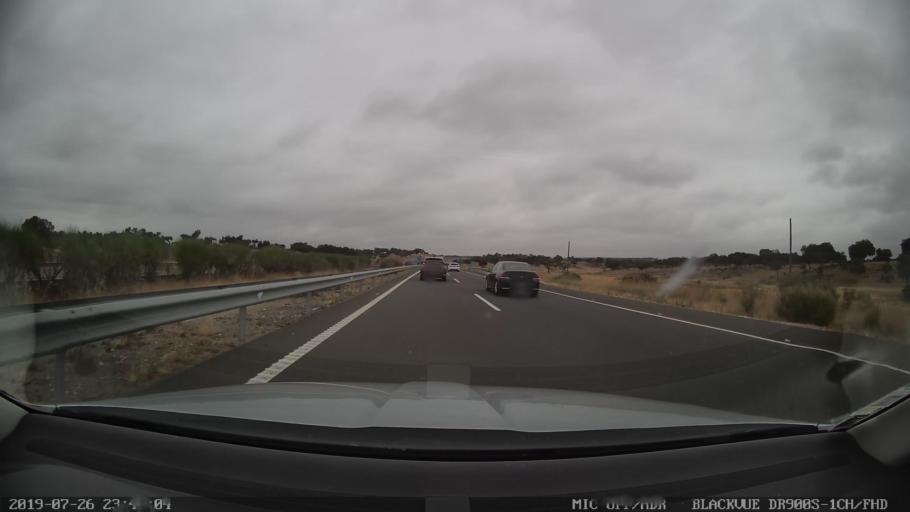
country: ES
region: Extremadura
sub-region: Provincia de Caceres
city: Jaraicejo
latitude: 39.6009
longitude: -5.8387
